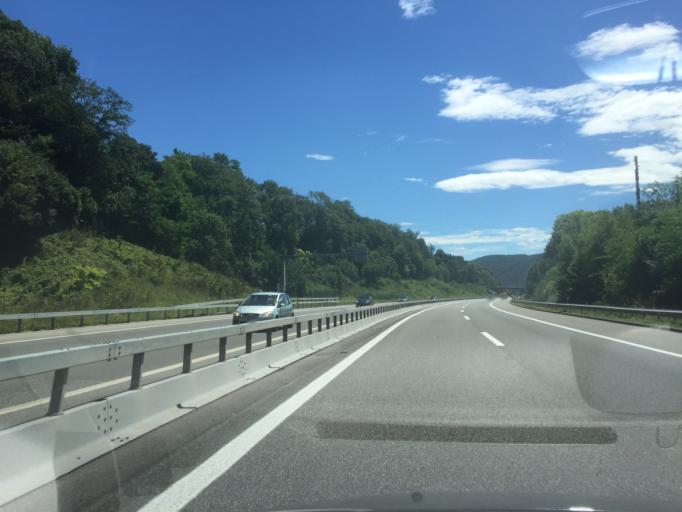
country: CH
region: Ticino
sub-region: Mendrisio District
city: Mendrisio
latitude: 45.8557
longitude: 8.9775
